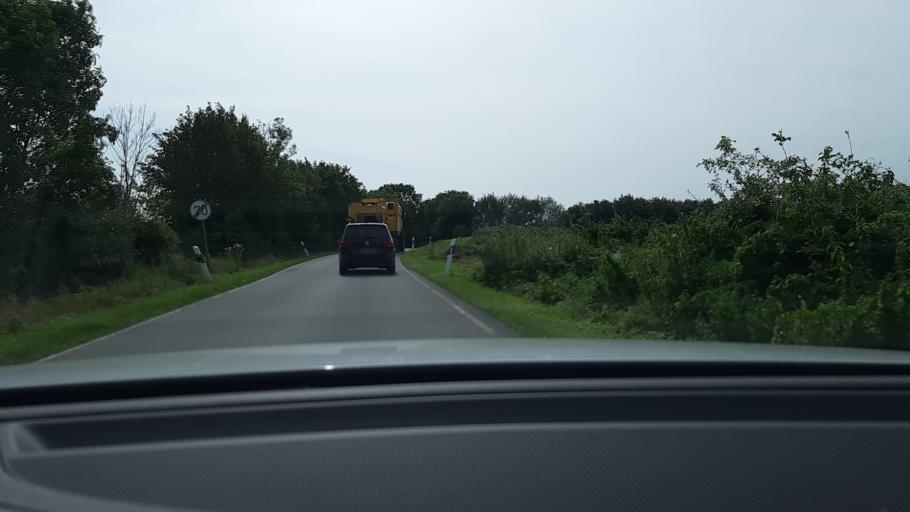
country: DE
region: Schleswig-Holstein
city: Rehhorst
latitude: 53.8652
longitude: 10.4684
